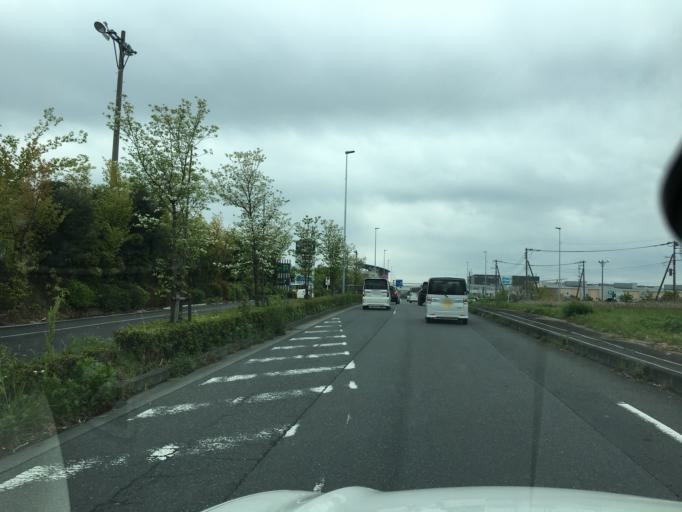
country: JP
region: Saitama
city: Yoshikawa
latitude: 35.8848
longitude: 139.8264
